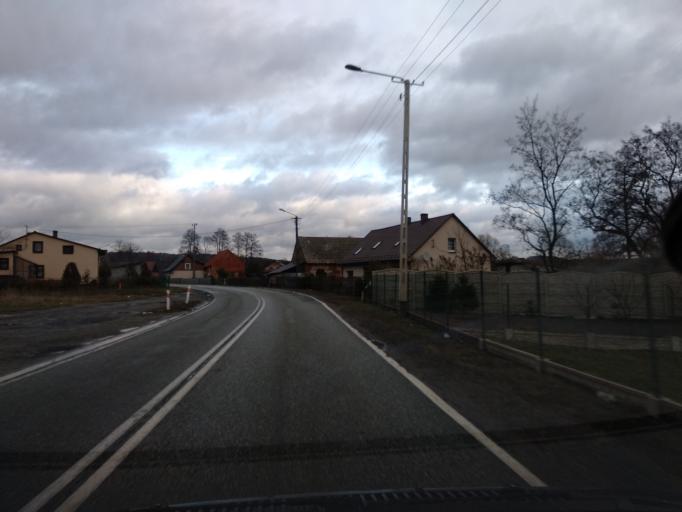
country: PL
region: Lower Silesian Voivodeship
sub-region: Powiat olesnicki
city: Miedzyborz
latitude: 51.3695
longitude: 17.6157
